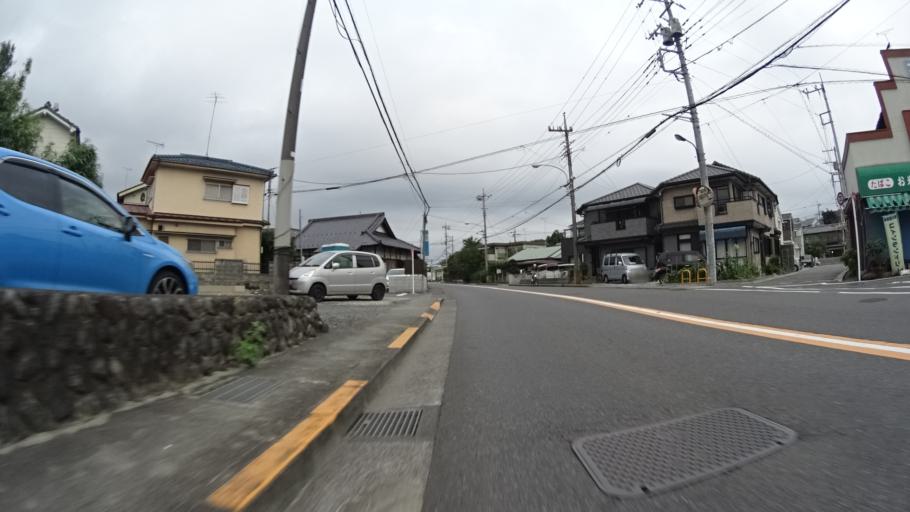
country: JP
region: Tokyo
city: Fussa
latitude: 35.7603
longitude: 139.3056
